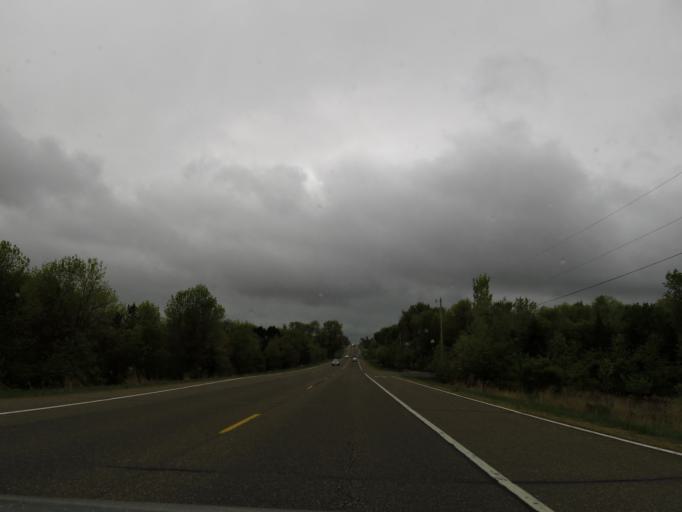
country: US
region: Minnesota
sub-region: Washington County
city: Oakdale
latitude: 44.9805
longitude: -92.9339
